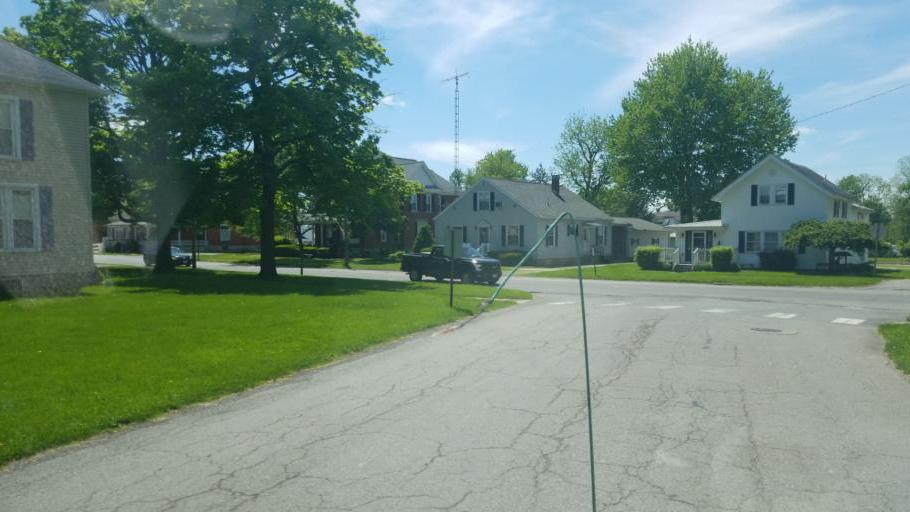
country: US
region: Ohio
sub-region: Huron County
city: Willard
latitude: 41.0664
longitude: -82.8863
